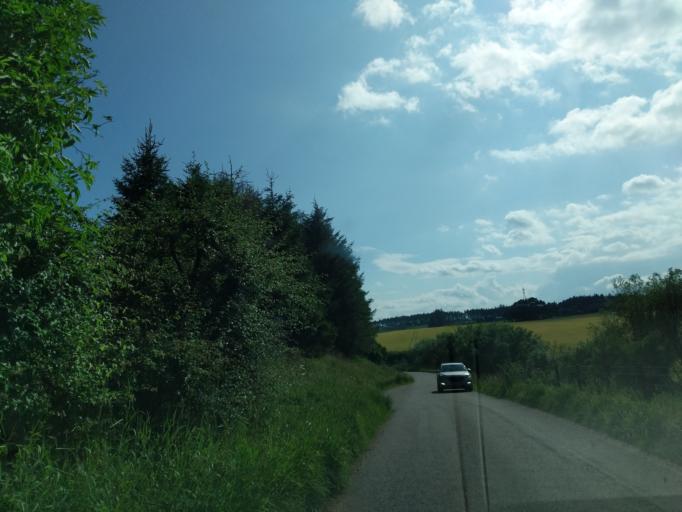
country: GB
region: Scotland
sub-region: Moray
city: Rothes
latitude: 57.4895
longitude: -3.2208
